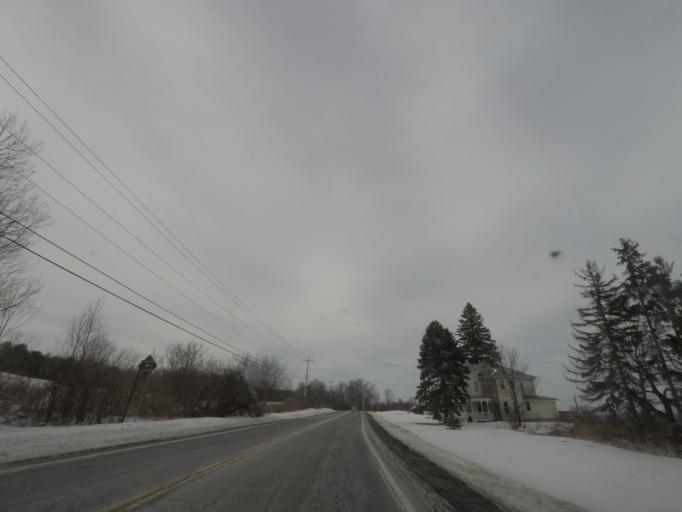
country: US
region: New York
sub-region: Albany County
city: Altamont
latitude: 42.6786
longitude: -74.0868
